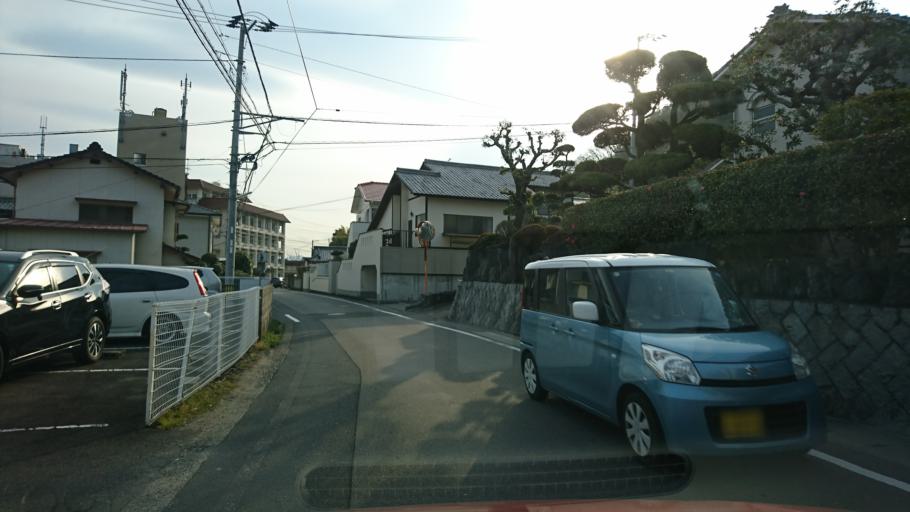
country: JP
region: Ehime
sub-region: Shikoku-chuo Shi
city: Matsuyama
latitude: 33.8576
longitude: 132.7767
